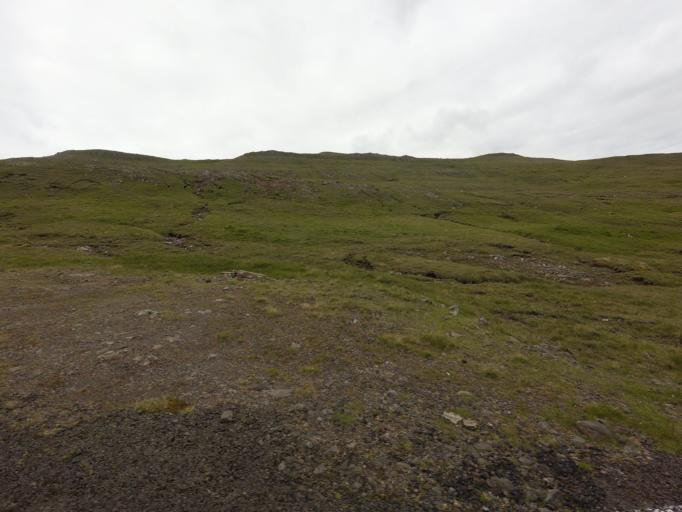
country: FO
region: Suduroy
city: Vagur
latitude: 61.4402
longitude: -6.7473
